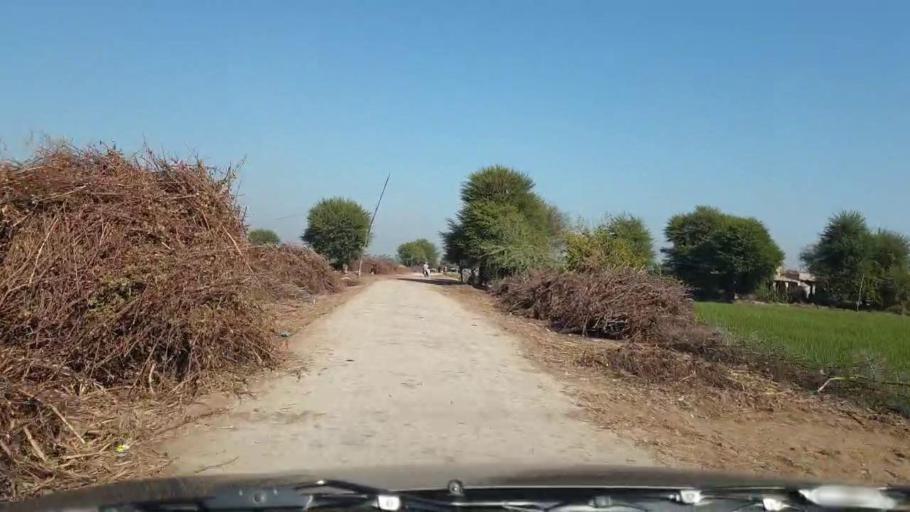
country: PK
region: Sindh
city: Jhol
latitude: 25.9463
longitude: 68.8193
